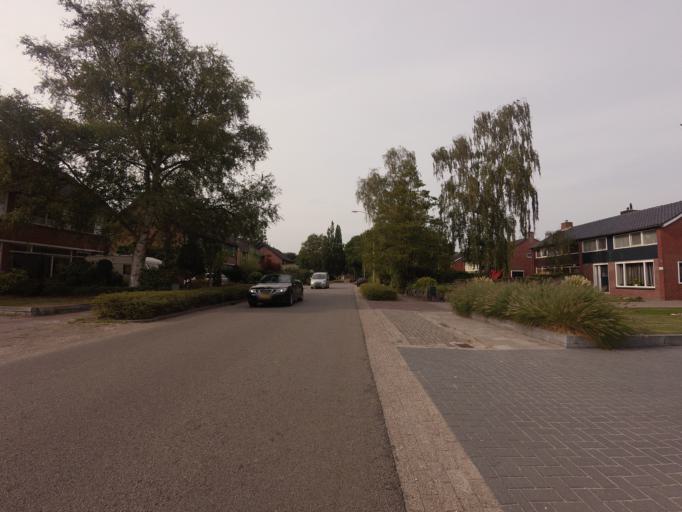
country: NL
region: Drenthe
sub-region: Gemeente Tynaarlo
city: Vries
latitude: 53.1309
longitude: 6.5660
